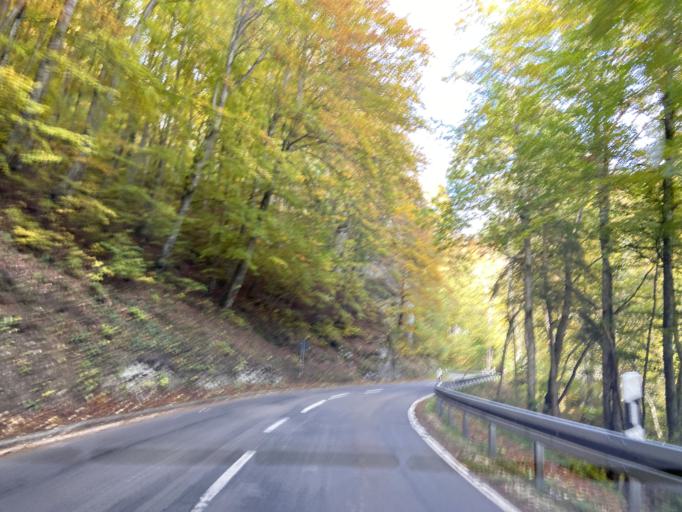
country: DE
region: Baden-Wuerttemberg
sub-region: Tuebingen Region
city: Schwenningen
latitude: 48.0888
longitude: 9.0311
